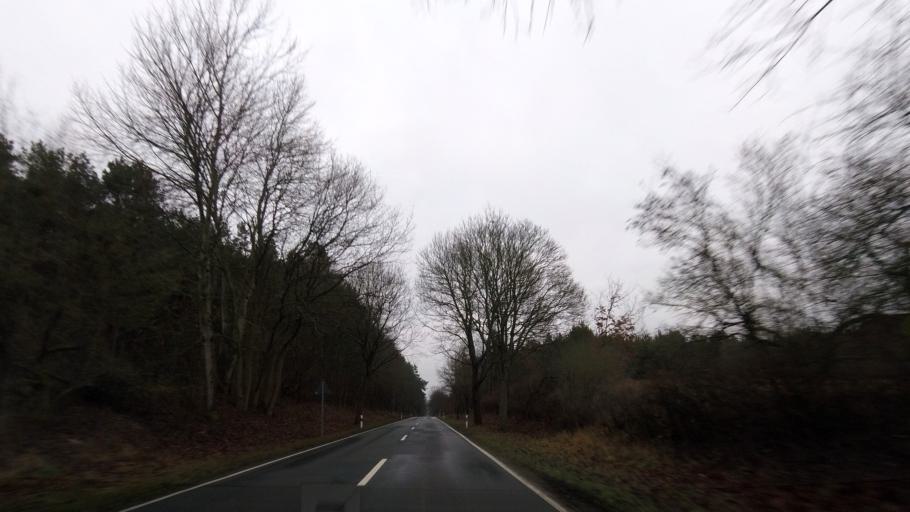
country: DE
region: Brandenburg
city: Treuenbrietzen
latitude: 52.0614
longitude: 12.9411
